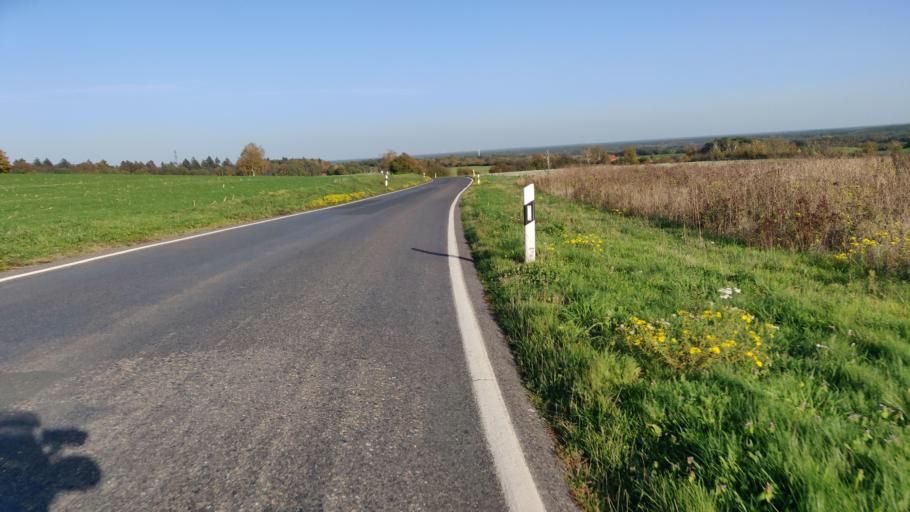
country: DE
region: Brandenburg
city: Grosskmehlen
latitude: 51.3616
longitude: 13.7304
